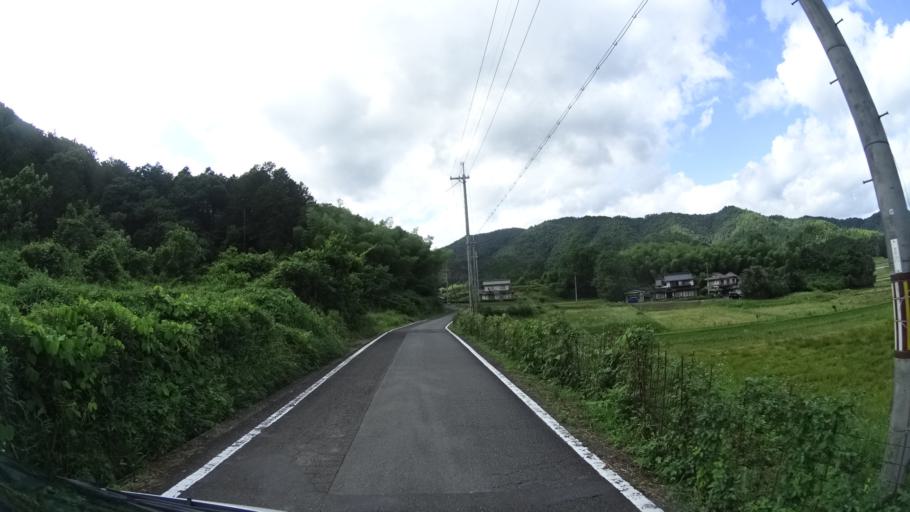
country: JP
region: Kyoto
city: Ayabe
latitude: 35.3591
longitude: 135.2066
